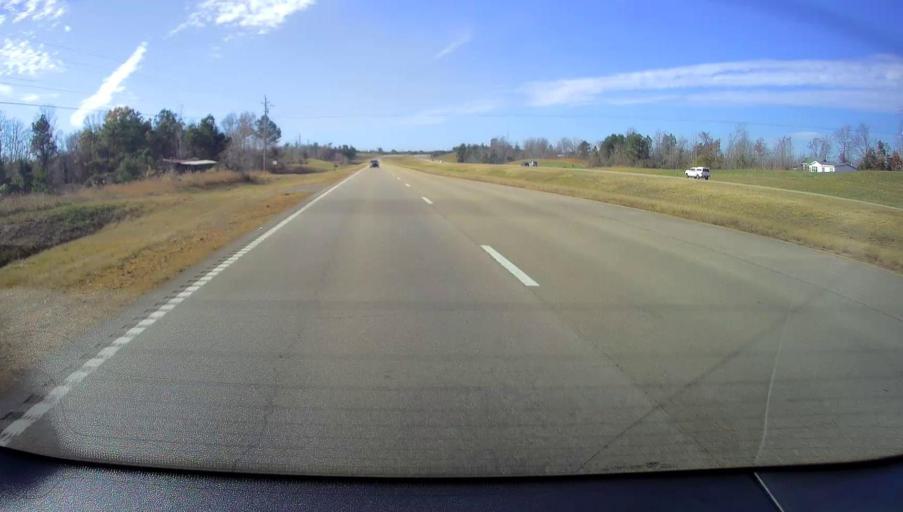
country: US
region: Mississippi
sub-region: Benton County
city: Ashland
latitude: 34.9542
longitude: -88.9962
